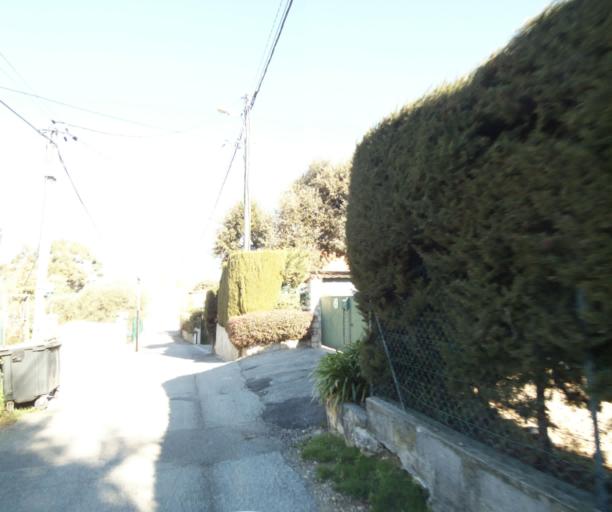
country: FR
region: Provence-Alpes-Cote d'Azur
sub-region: Departement des Alpes-Maritimes
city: Biot
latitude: 43.6074
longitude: 7.1020
